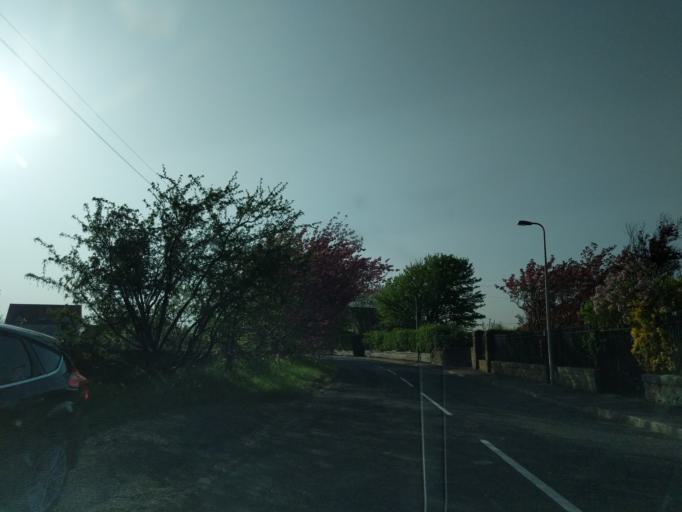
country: GB
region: Scotland
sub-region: Midlothian
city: Dalkeith
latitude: 55.8873
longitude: -3.0330
